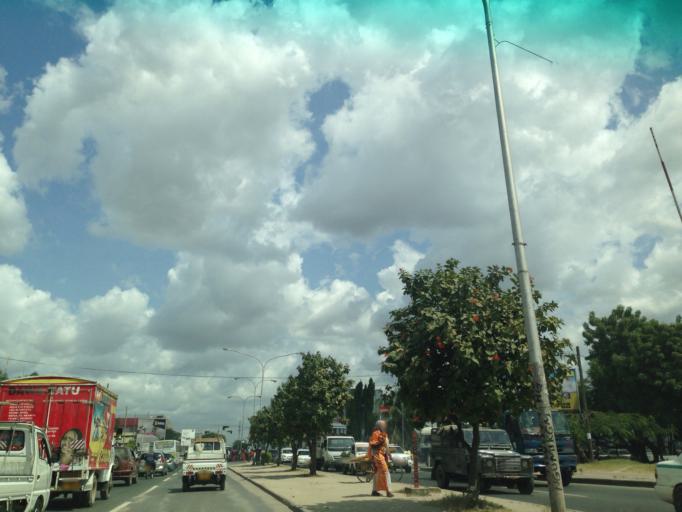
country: TZ
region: Dar es Salaam
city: Dar es Salaam
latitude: -6.8269
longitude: 39.2772
